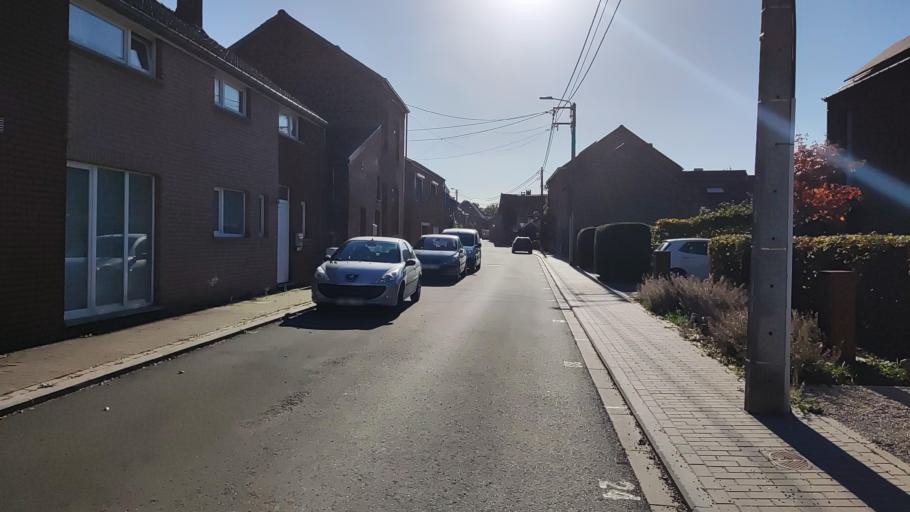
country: BE
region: Flanders
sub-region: Provincie Vlaams-Brabant
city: Hoegaarden
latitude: 50.7593
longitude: 4.8878
